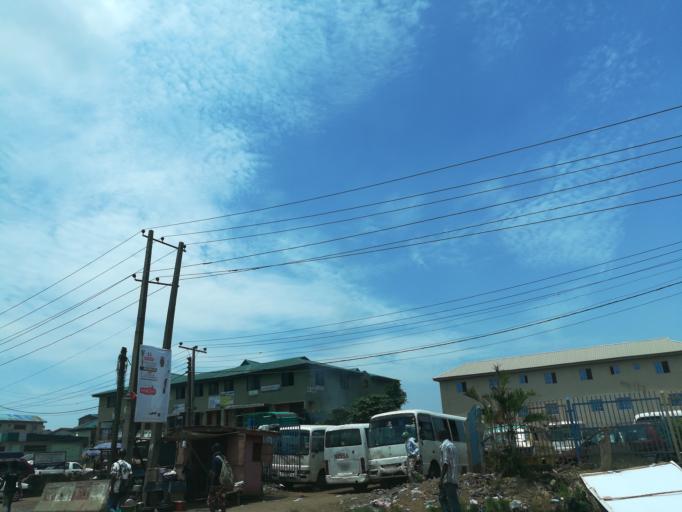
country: NG
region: Lagos
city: Ikorodu
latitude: 6.6239
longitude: 3.5049
